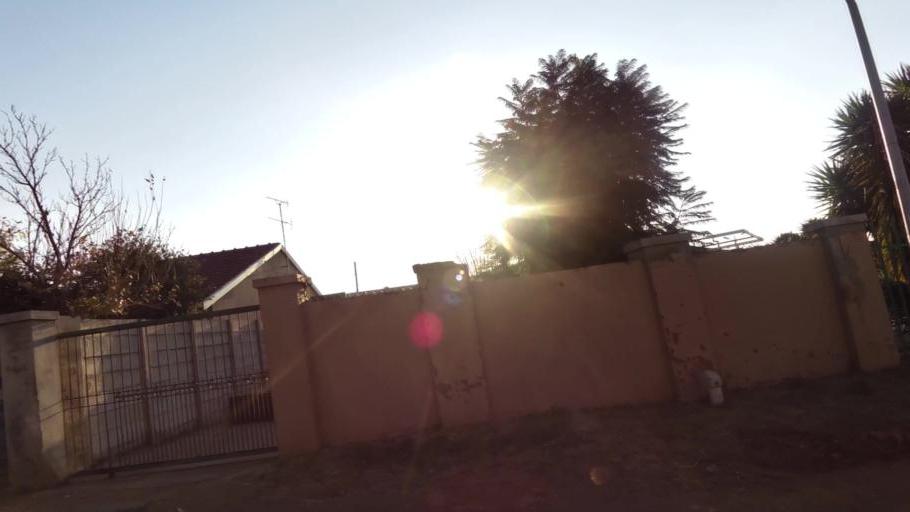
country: ZA
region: Gauteng
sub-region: City of Johannesburg Metropolitan Municipality
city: Johannesburg
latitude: -26.1740
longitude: 27.9725
